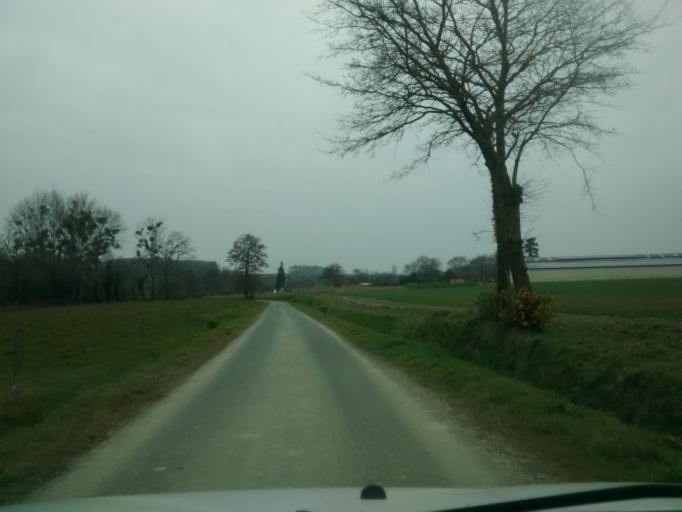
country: FR
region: Brittany
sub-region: Departement d'Ille-et-Vilaine
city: Bazouges-la-Perouse
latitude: 48.3853
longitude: -1.5554
